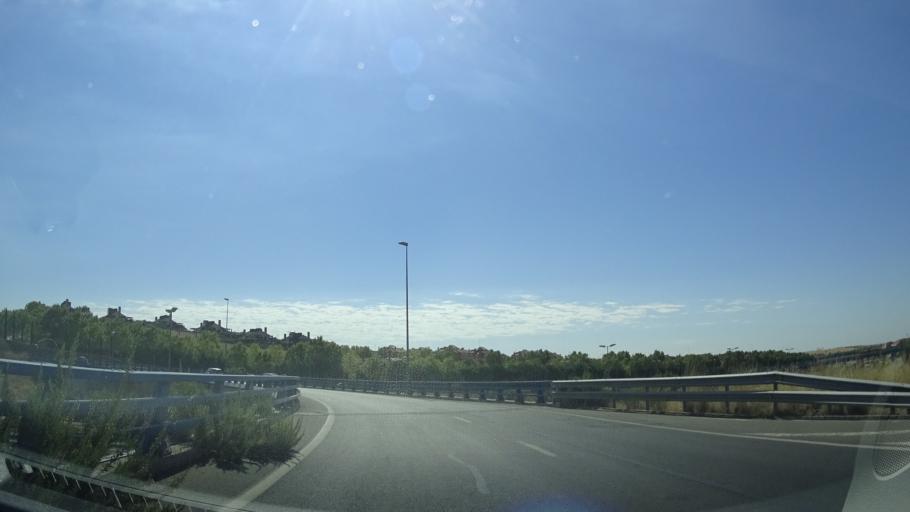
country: ES
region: Madrid
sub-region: Provincia de Madrid
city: Boadilla del Monte
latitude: 40.4117
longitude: -3.8897
